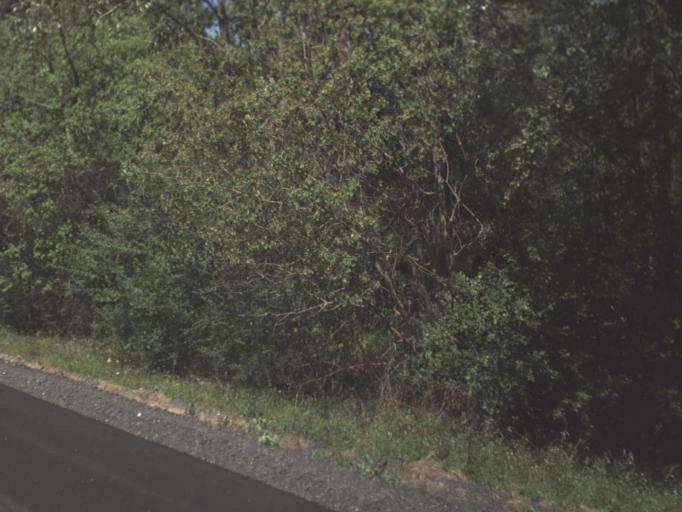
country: US
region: Florida
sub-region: Escambia County
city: Myrtle Grove
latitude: 30.4158
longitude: -87.3174
